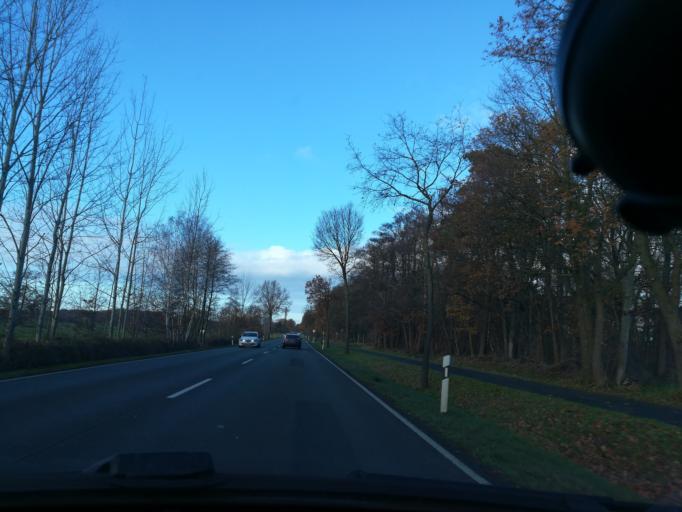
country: DE
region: Lower Saxony
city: Raddestorf
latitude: 52.4453
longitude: 8.9301
